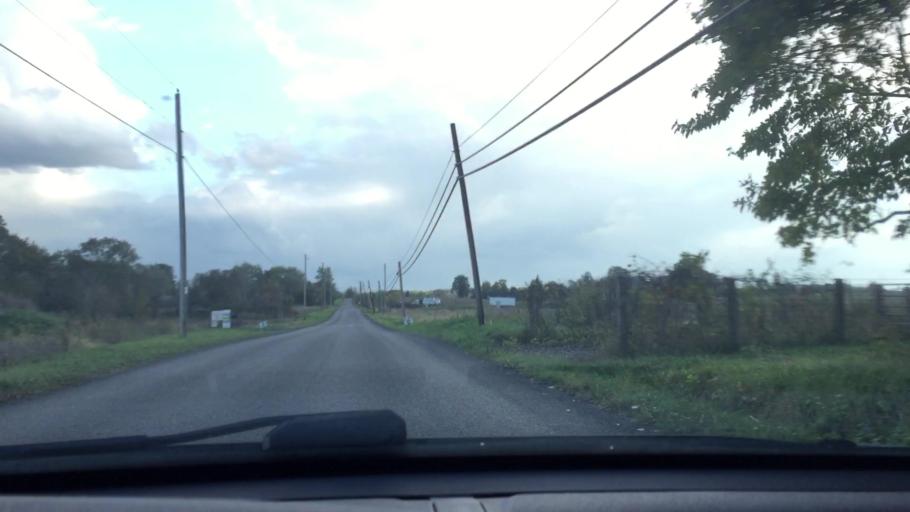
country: US
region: Pennsylvania
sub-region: Lawrence County
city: Bessemer
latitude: 40.9877
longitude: -80.4565
